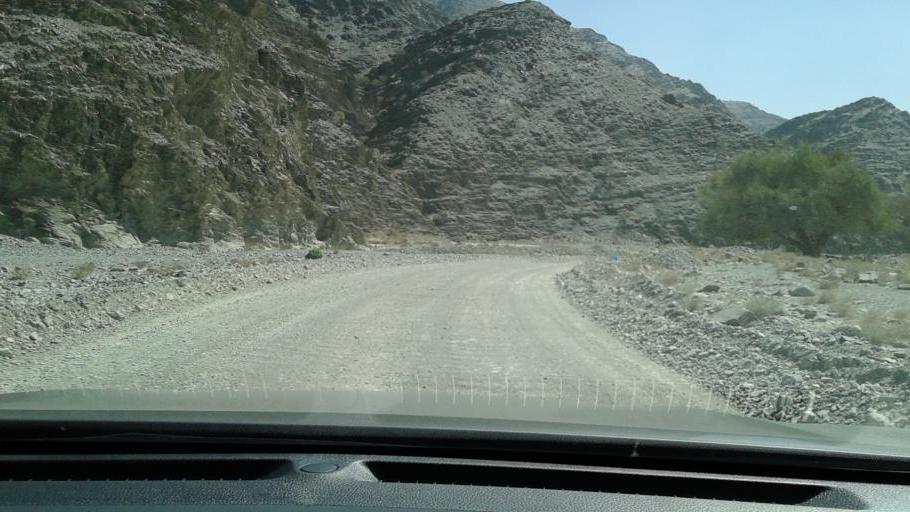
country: OM
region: Al Batinah
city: Bayt al `Awabi
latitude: 23.2646
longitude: 57.4467
